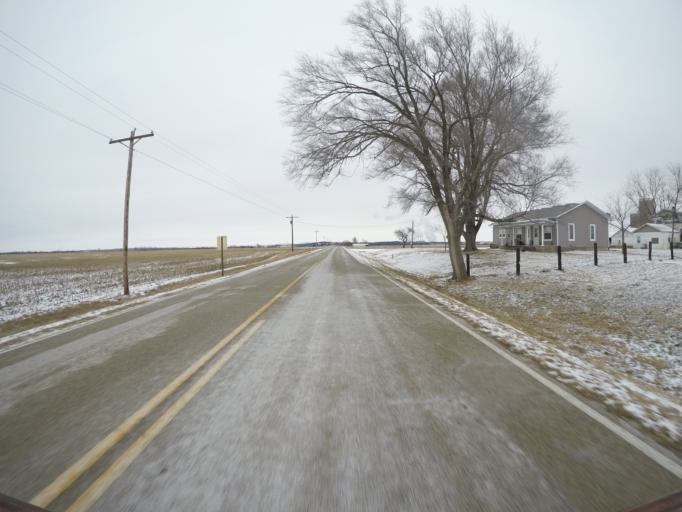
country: US
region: Kansas
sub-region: Pottawatomie County
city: Saint Marys
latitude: 39.2029
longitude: -96.1475
